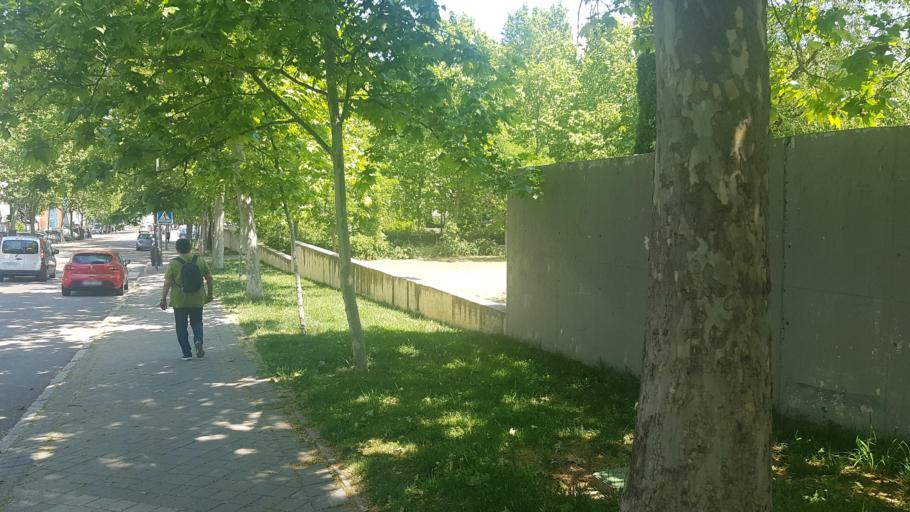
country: ES
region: Madrid
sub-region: Provincia de Madrid
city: Usera
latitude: 40.3703
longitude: -3.7122
